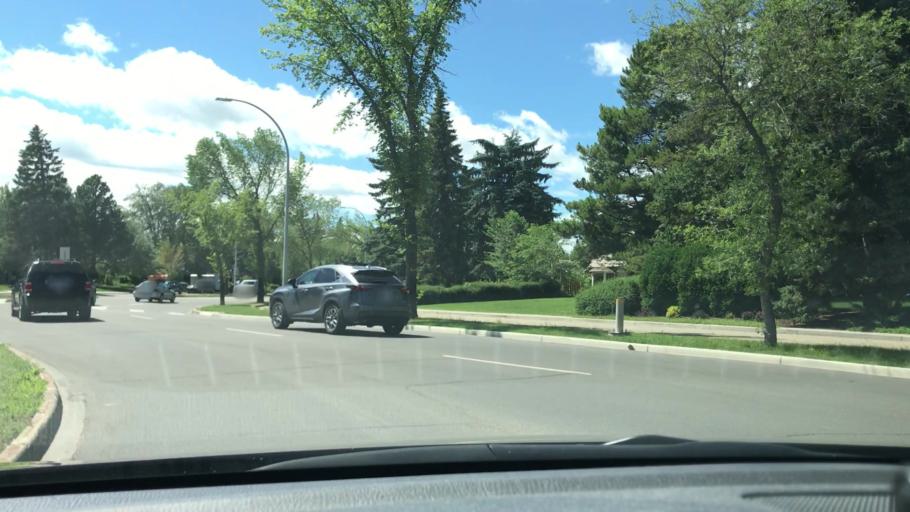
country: CA
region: Alberta
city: Edmonton
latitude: 53.5197
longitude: -113.5658
